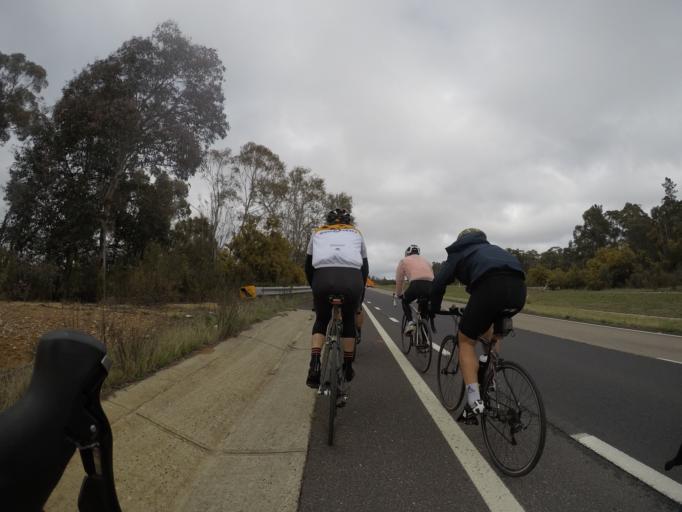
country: AU
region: New South Wales
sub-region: Lithgow
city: Lithgow
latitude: -33.4341
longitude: 150.0720
